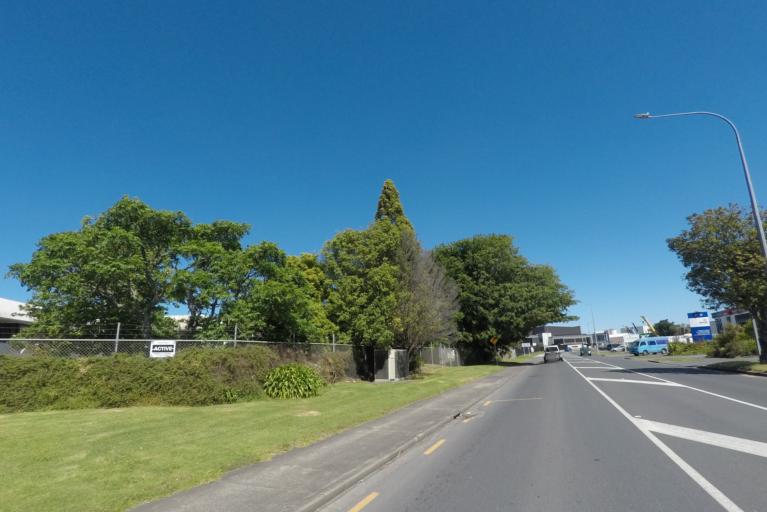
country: NZ
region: Auckland
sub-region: Auckland
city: Rosebank
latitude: -36.8720
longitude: 174.6682
